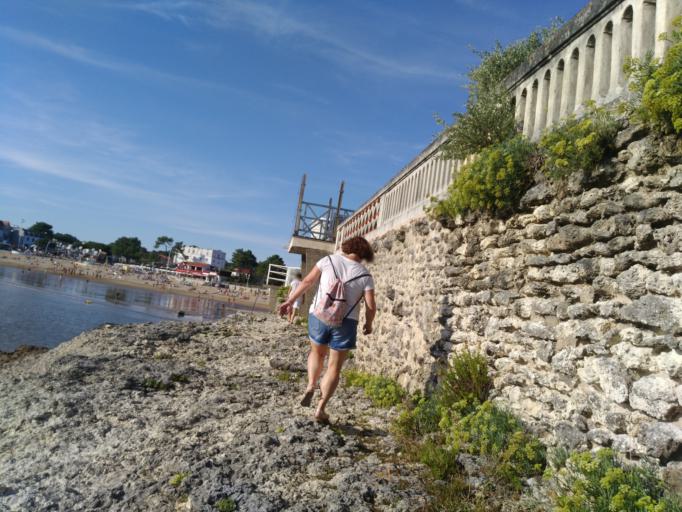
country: FR
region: Poitou-Charentes
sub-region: Departement de la Charente-Maritime
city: Saint-Palais-sur-Mer
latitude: 45.6396
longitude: -1.0874
